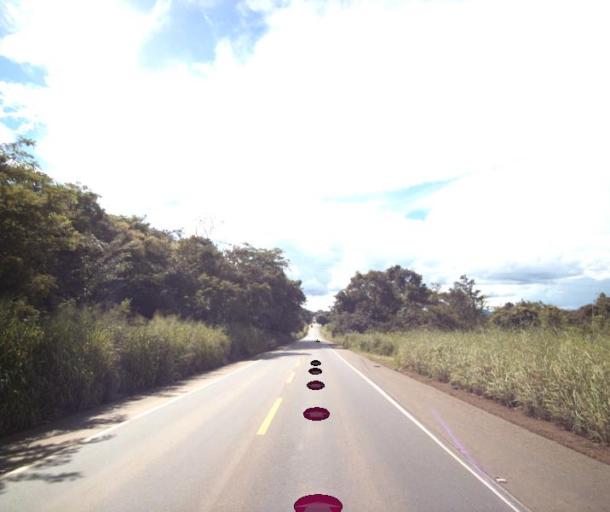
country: BR
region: Goias
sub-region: Jaragua
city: Jaragua
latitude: -15.7908
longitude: -49.3021
